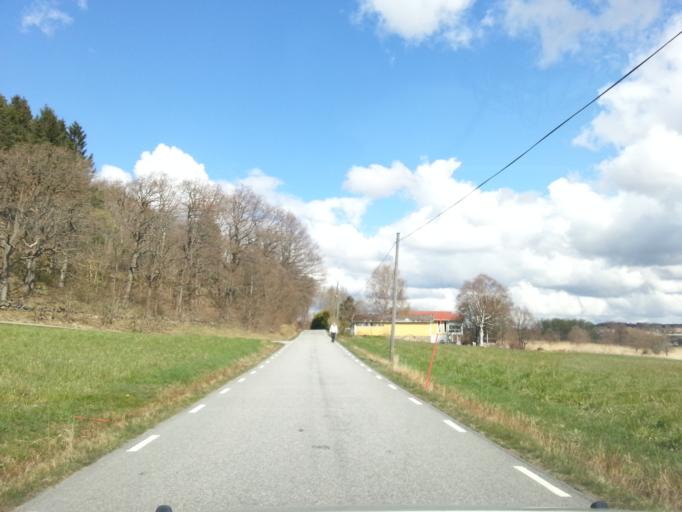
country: SE
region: Vaestra Goetaland
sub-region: Kungalvs Kommun
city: Kungalv
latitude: 57.8606
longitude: 11.9540
